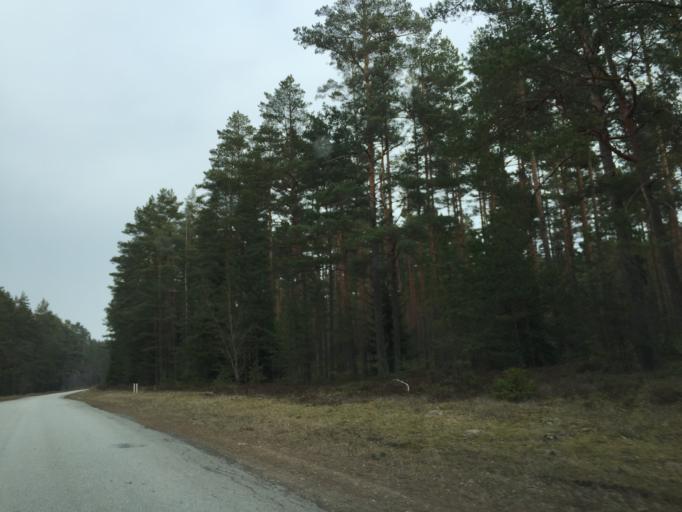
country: LV
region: Salacgrivas
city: Ainazi
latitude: 57.9826
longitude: 24.4172
